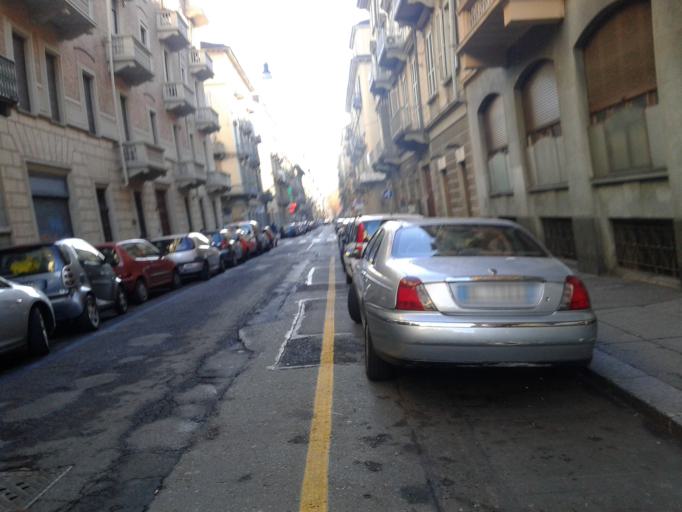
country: IT
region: Piedmont
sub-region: Provincia di Torino
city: Turin
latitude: 45.0607
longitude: 7.6799
